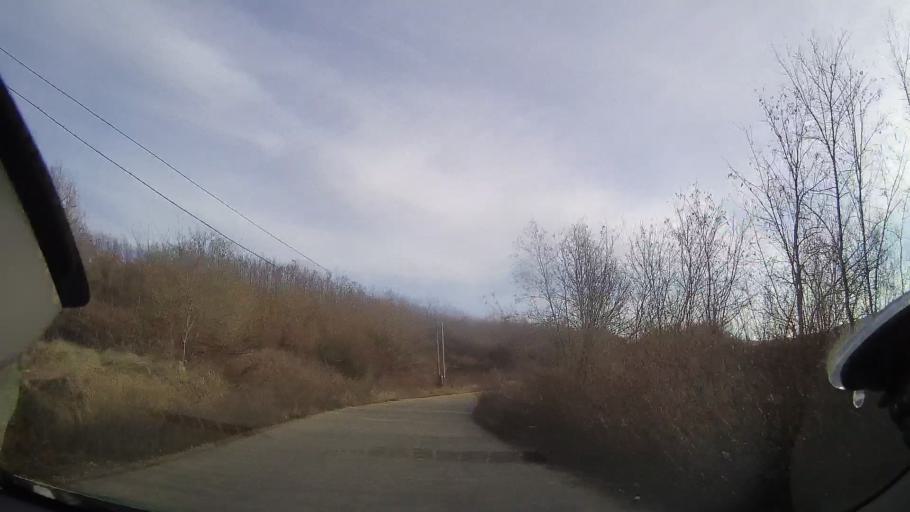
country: RO
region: Bihor
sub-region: Comuna Sarbi
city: Sarbi
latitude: 47.1870
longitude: 22.1276
